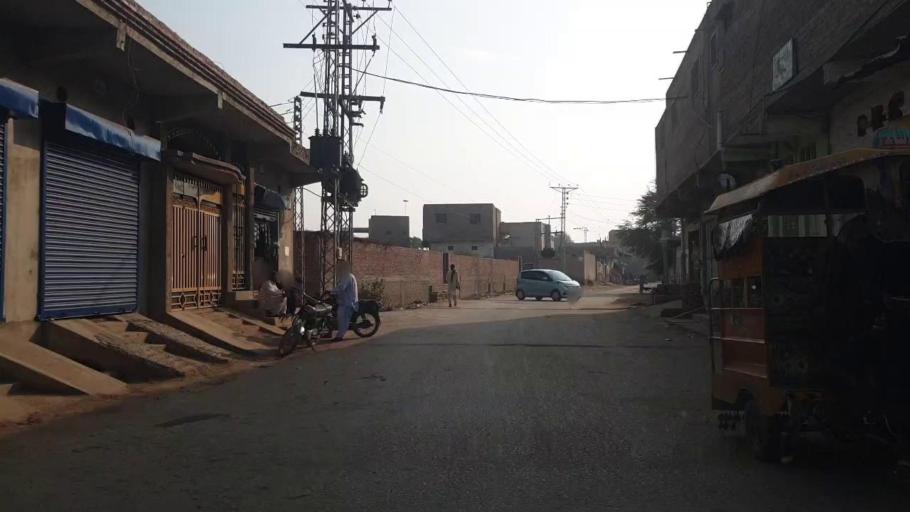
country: PK
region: Sindh
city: Hala
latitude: 25.7929
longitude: 68.3914
